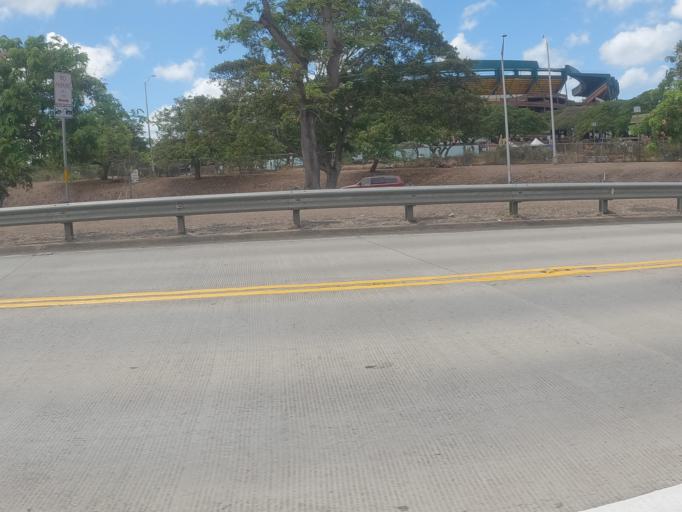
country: US
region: Hawaii
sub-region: Honolulu County
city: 'Aiea
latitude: 21.3755
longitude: -157.9315
